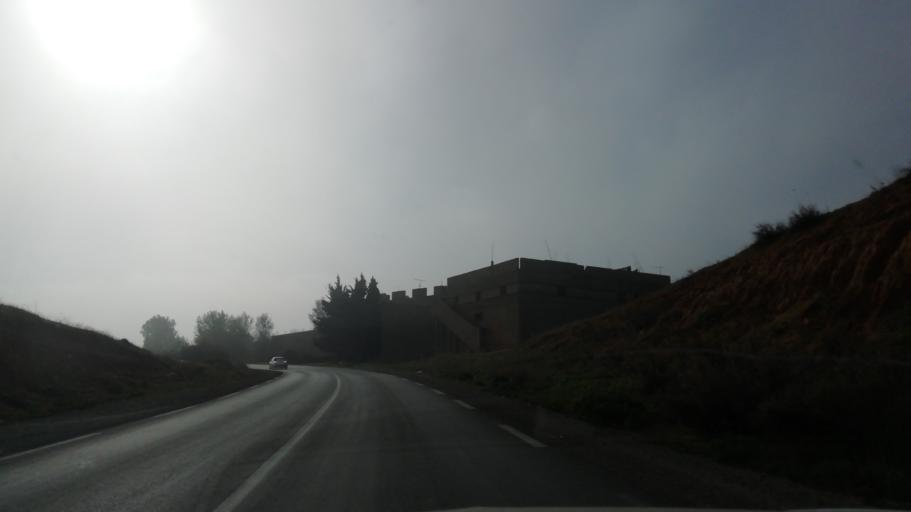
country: DZ
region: Mascara
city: Mascara
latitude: 35.5333
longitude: 0.3535
